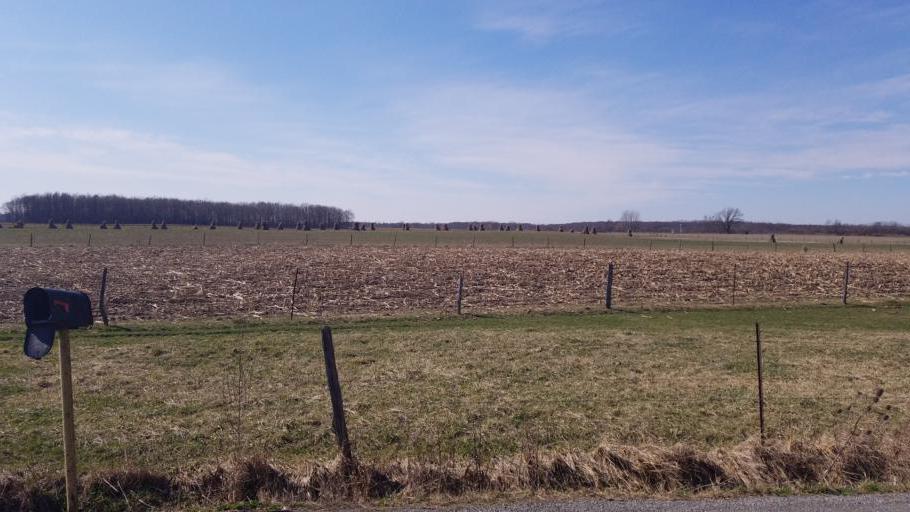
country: US
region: Ohio
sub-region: Hardin County
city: Kenton
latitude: 40.5558
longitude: -83.4406
